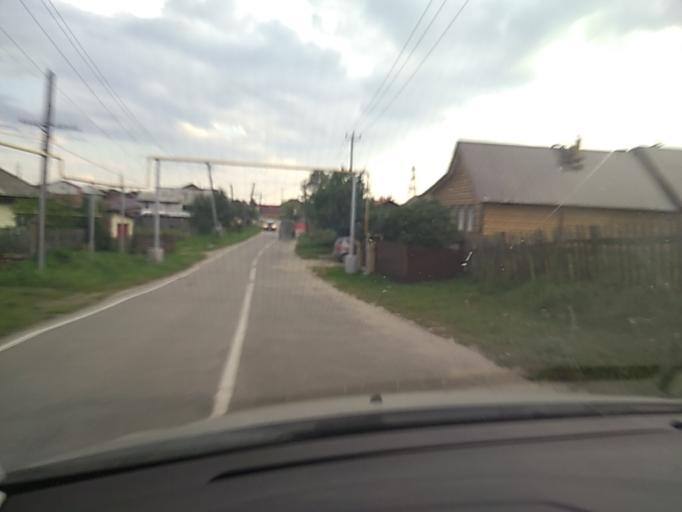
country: RU
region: Chelyabinsk
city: Kyshtym
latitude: 55.6957
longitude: 60.5315
